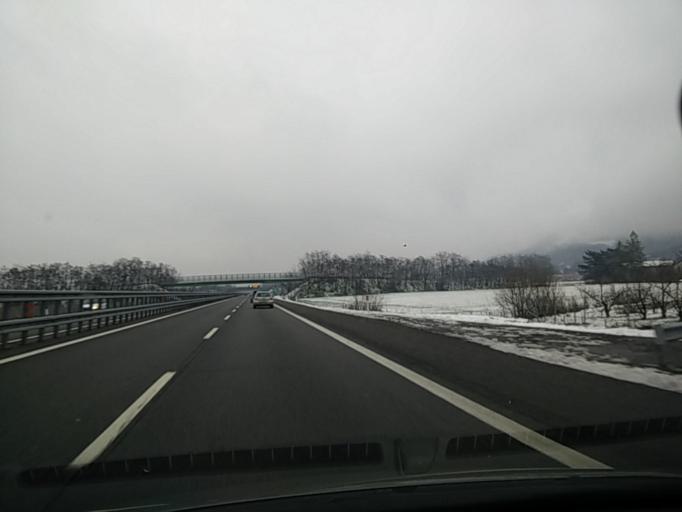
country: IT
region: Lombardy
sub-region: Provincia di Pavia
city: Broni
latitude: 45.0734
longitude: 9.2500
